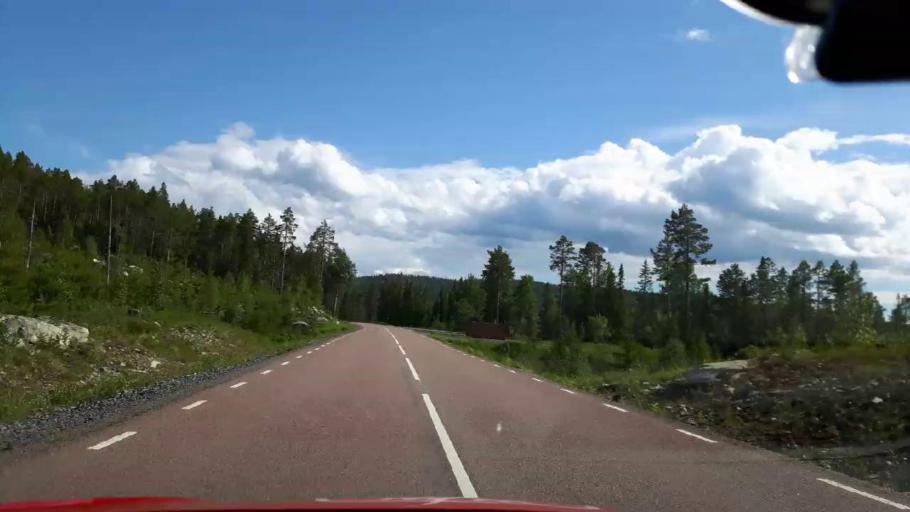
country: SE
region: Jaemtland
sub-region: Krokoms Kommun
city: Valla
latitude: 64.0329
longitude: 14.1904
